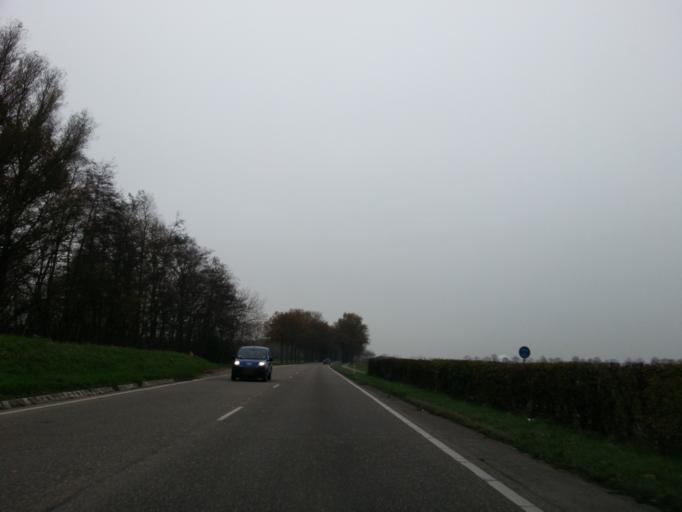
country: NL
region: North Brabant
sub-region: Gemeente Steenbergen
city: Steenbergen
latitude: 51.5690
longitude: 4.3094
